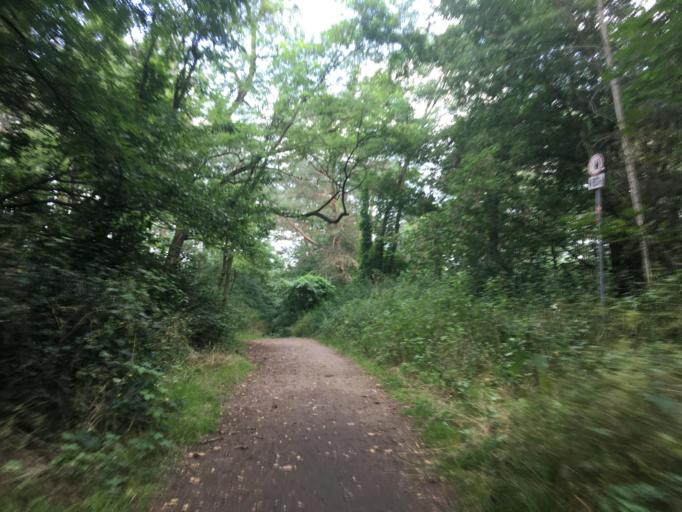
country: DE
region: Brandenburg
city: Wildau
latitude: 52.3312
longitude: 13.6226
